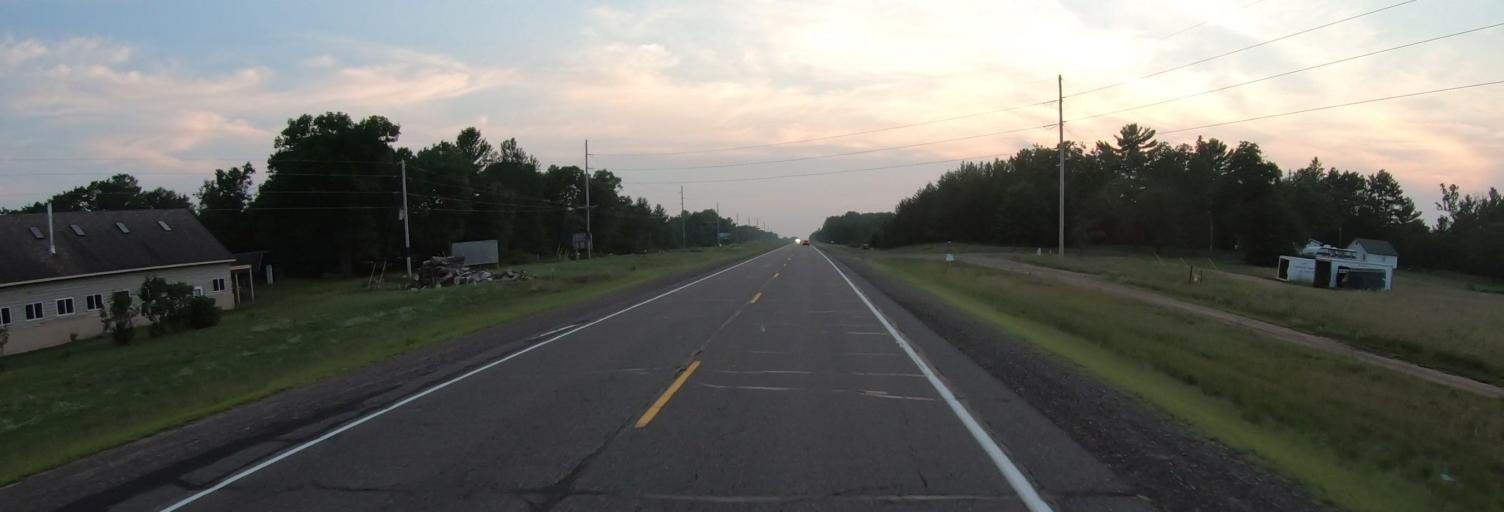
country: US
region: Wisconsin
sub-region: Burnett County
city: Grantsburg
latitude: 45.7732
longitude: -92.7350
